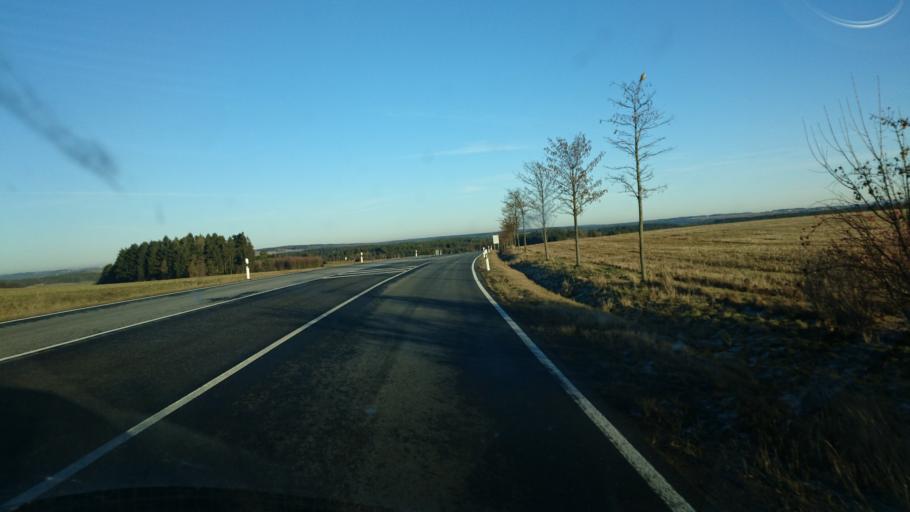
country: DE
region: Thuringia
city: Kirschkau
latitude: 50.5993
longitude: 11.8948
